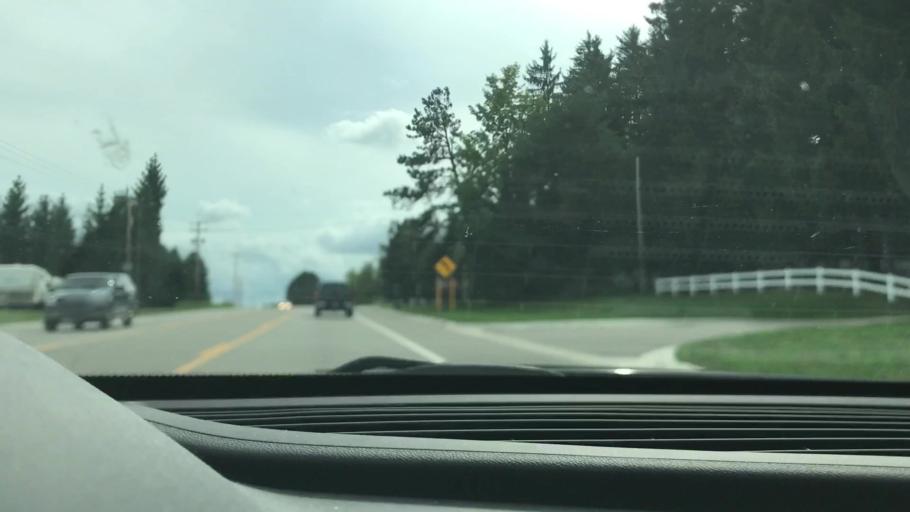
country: US
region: Michigan
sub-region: Missaukee County
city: Lake City
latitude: 44.3164
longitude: -85.2137
